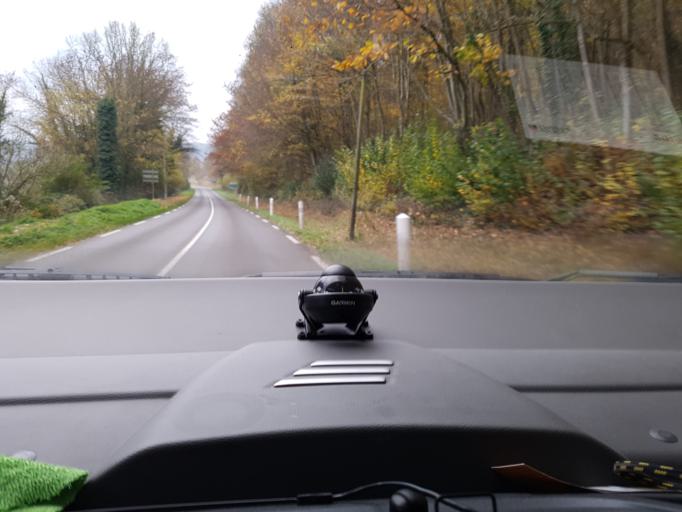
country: FR
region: Haute-Normandie
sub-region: Departement de la Seine-Maritime
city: Eu
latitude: 50.0641
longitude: 1.4226
